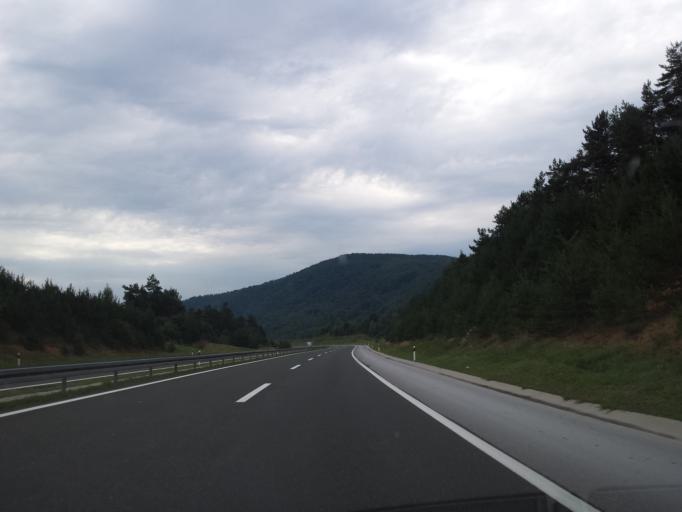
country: HR
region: Karlovacka
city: Ostarije
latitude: 45.2006
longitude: 15.2653
